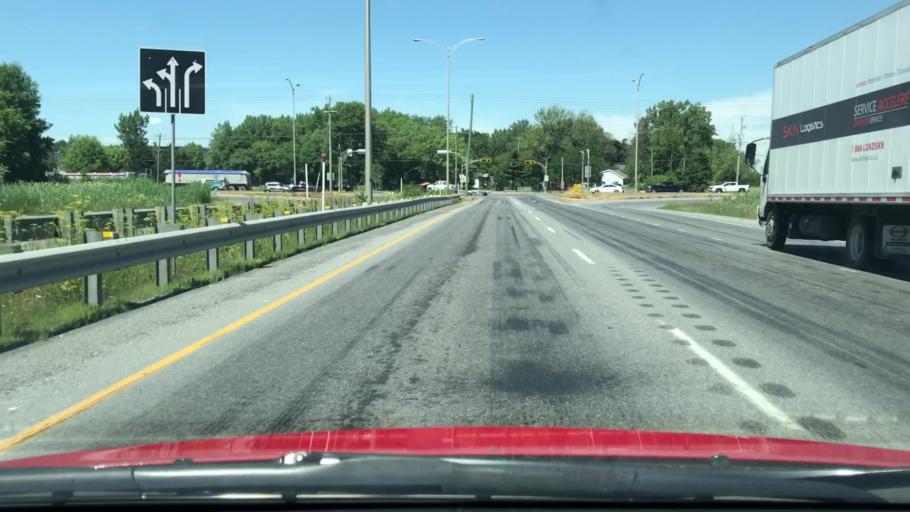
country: CA
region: Quebec
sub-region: Monteregie
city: Saint-Constant
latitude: 45.3941
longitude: -73.6034
